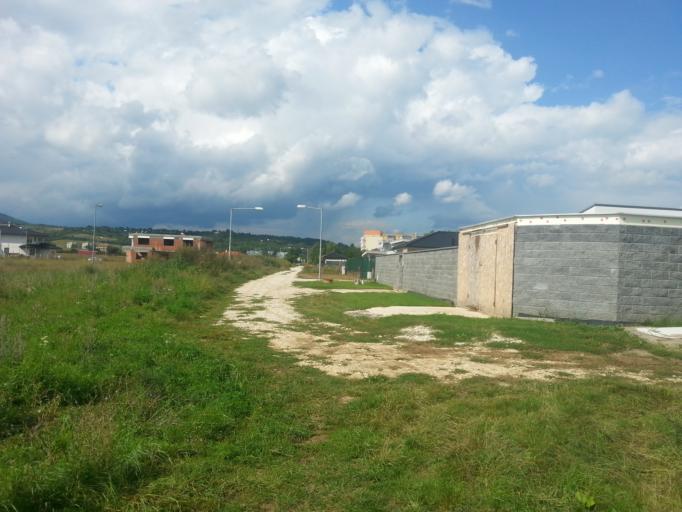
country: SK
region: Trenciansky
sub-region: Okres Nove Mesto nad Vahom
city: Nove Mesto nad Vahom
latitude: 48.7483
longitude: 17.8215
